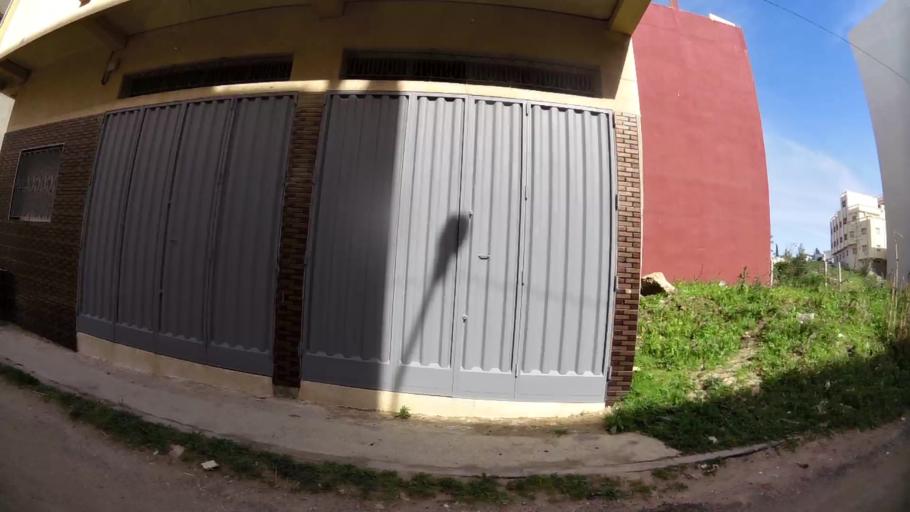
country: MA
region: Tanger-Tetouan
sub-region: Tanger-Assilah
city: Tangier
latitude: 35.7678
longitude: -5.7736
